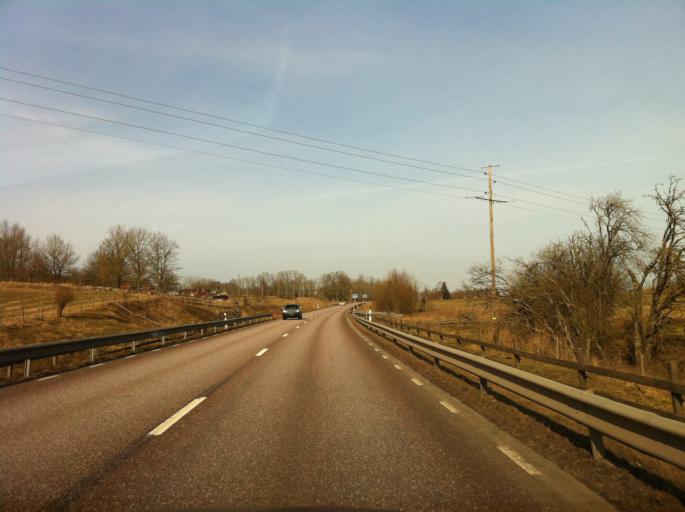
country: SE
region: Vaestra Goetaland
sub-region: Skovde Kommun
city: Skultorp
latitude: 58.2889
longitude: 13.8050
